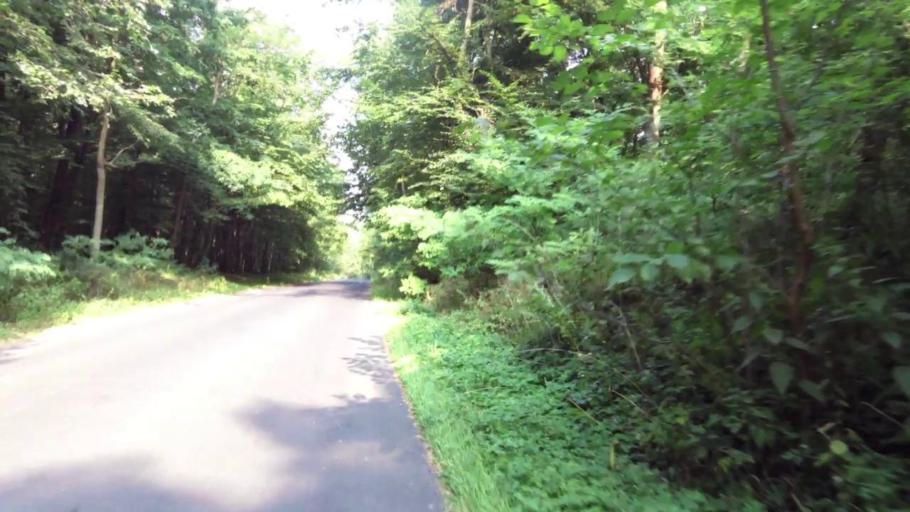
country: PL
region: West Pomeranian Voivodeship
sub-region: Powiat mysliborski
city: Debno
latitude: 52.8516
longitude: 14.6995
